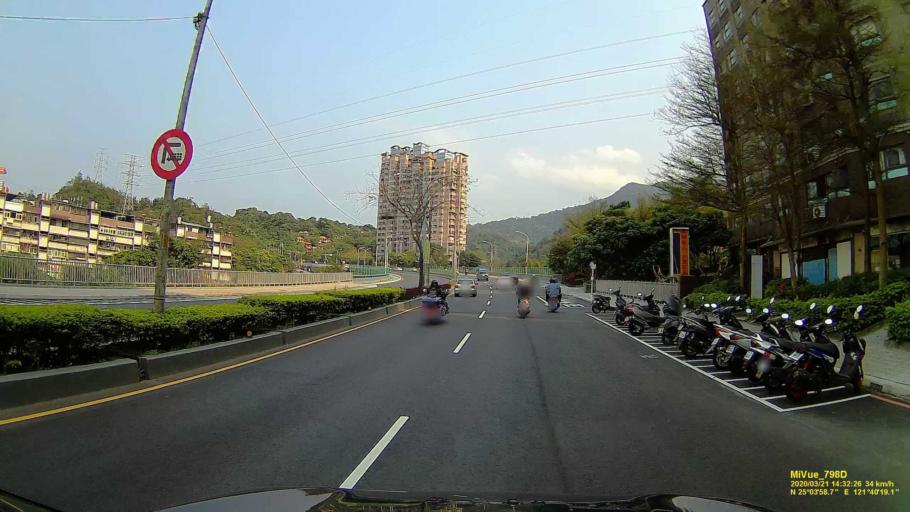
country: TW
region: Taiwan
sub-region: Keelung
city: Keelung
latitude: 25.0661
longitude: 121.6721
